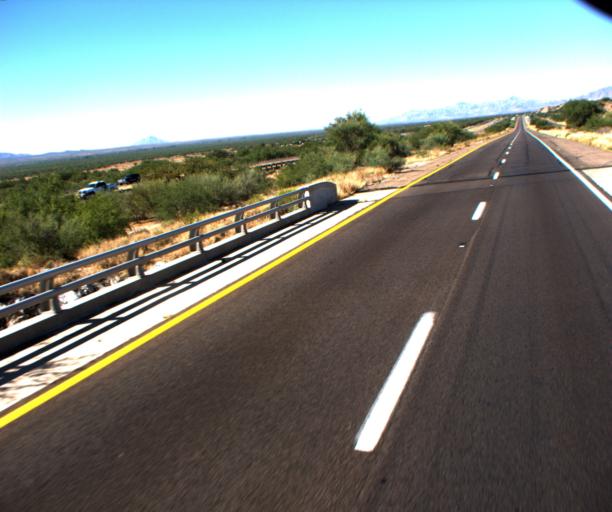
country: US
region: Arizona
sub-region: Pima County
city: Green Valley
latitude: 31.8041
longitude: -111.0143
